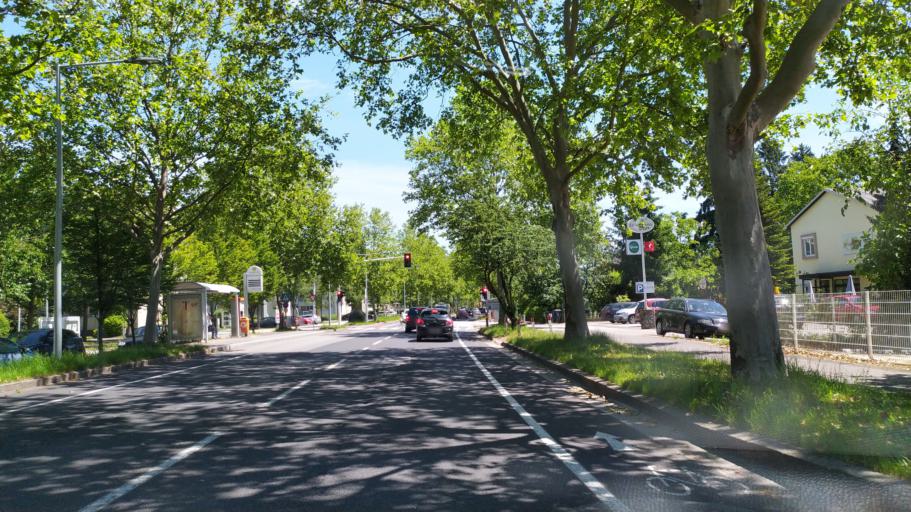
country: AT
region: Upper Austria
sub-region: Politischer Bezirk Linz-Land
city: Ansfelden
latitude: 48.2534
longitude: 14.3042
